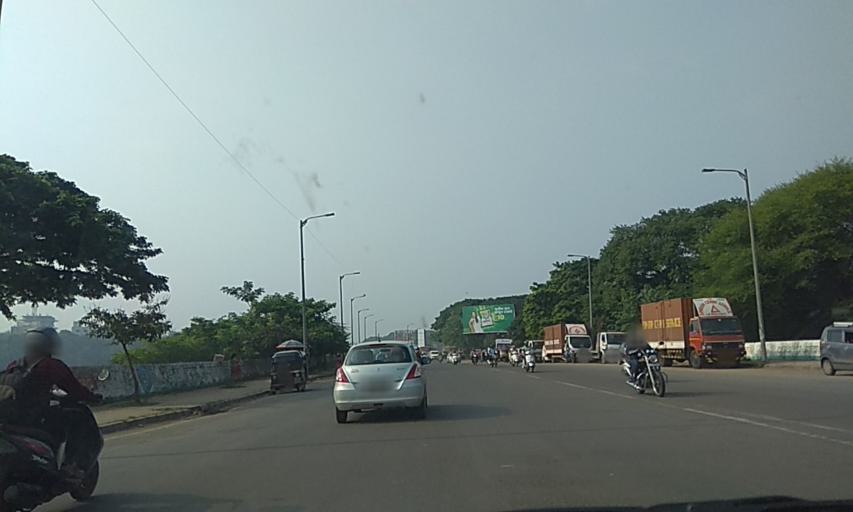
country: IN
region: Maharashtra
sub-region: Pune Division
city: Shivaji Nagar
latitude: 18.5355
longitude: 73.8619
